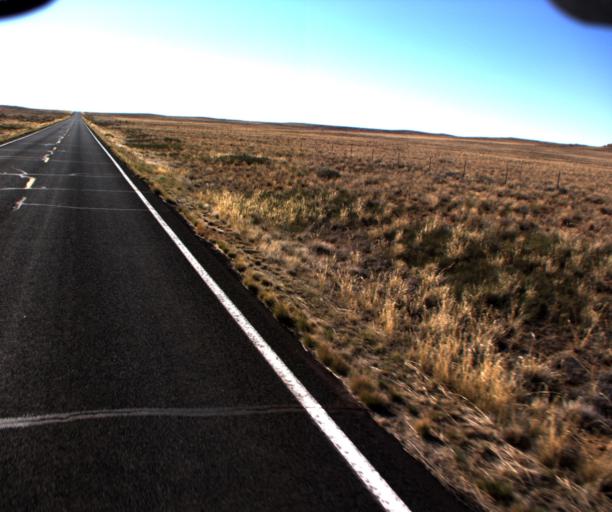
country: US
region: Arizona
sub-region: Navajo County
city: First Mesa
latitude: 35.6520
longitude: -110.4898
